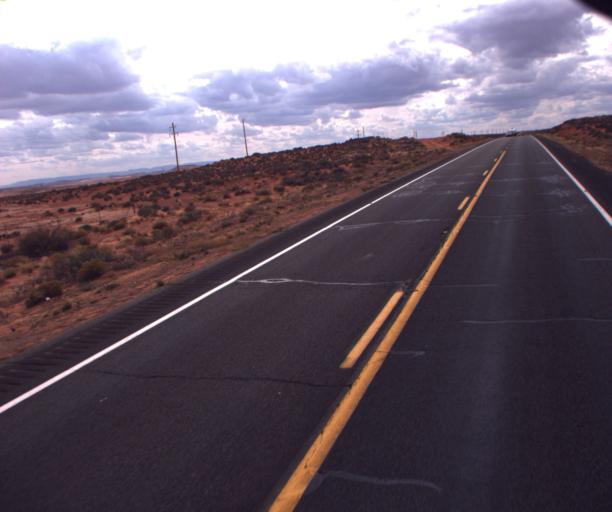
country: US
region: Arizona
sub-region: Navajo County
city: Kayenta
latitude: 36.9275
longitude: -109.7536
